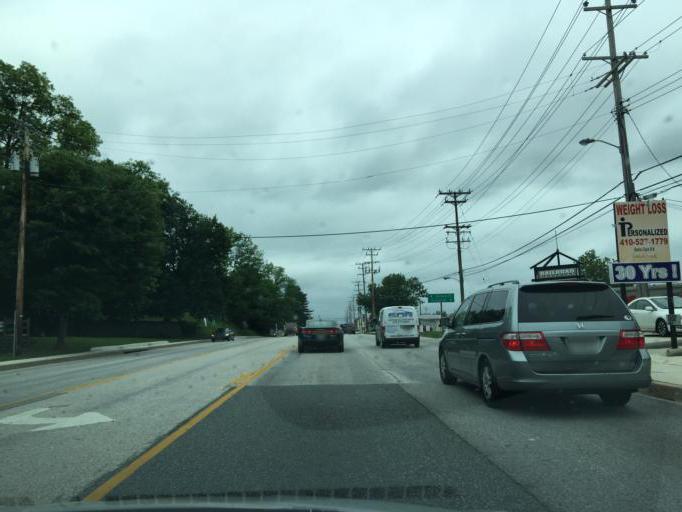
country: US
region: Maryland
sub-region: Baltimore County
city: Cockeysville
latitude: 39.4849
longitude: -76.6455
